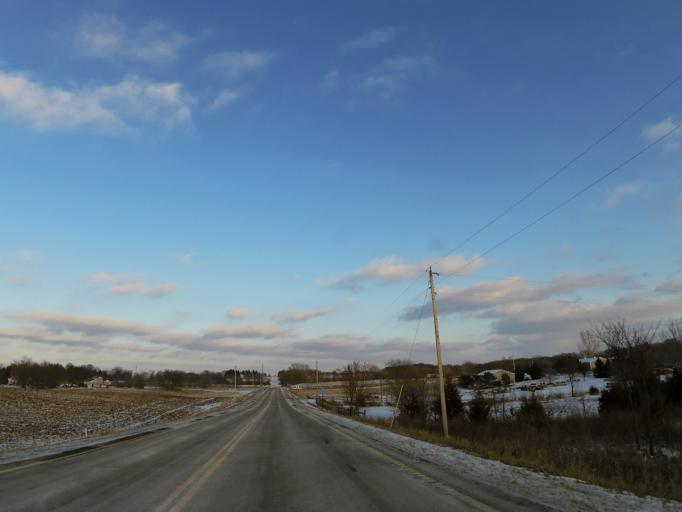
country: US
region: Minnesota
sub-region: Scott County
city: Prior Lake
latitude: 44.6596
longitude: -93.4446
